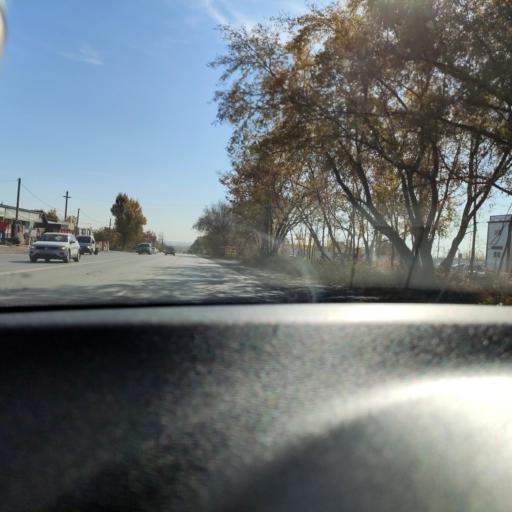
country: RU
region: Samara
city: Petra-Dubrava
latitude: 53.2666
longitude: 50.2825
